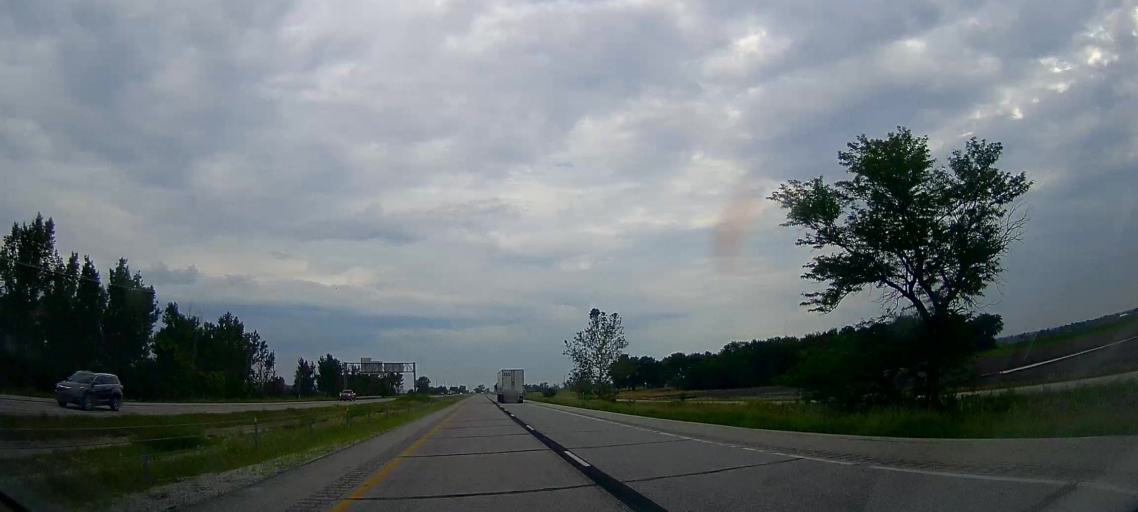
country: US
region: Iowa
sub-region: Harrison County
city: Missouri Valley
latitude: 41.4803
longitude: -95.9002
